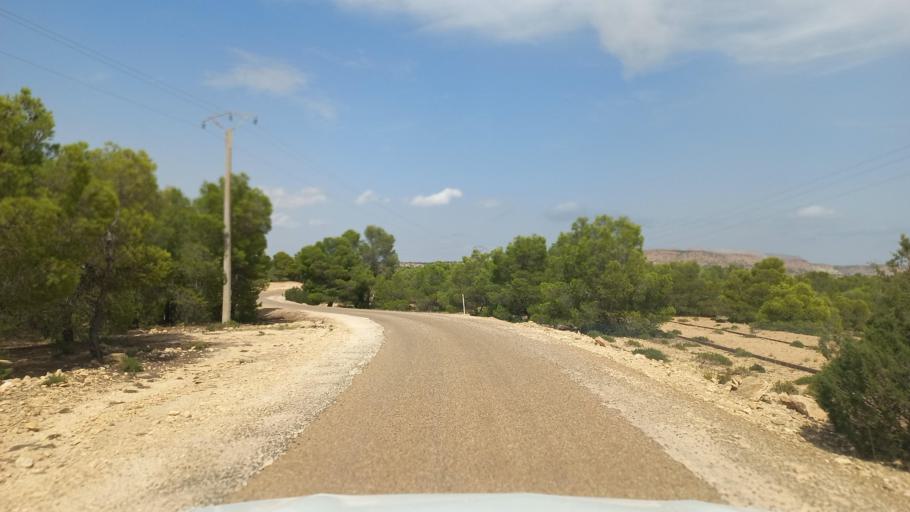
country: TN
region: Al Qasrayn
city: Sbiba
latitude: 35.3973
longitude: 8.9144
